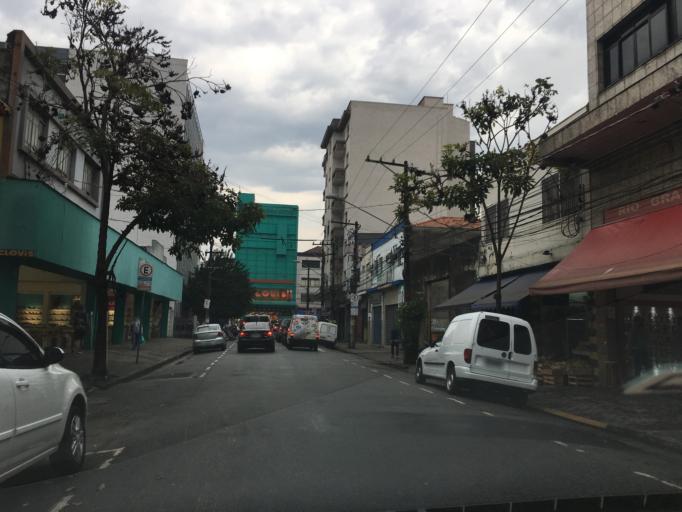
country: BR
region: Sao Paulo
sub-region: Sao Paulo
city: Sao Paulo
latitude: -23.5426
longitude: -46.6143
